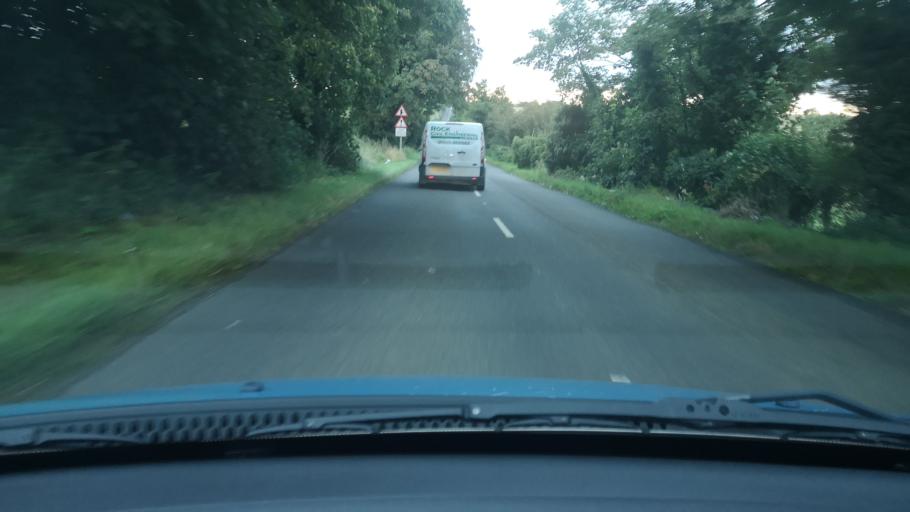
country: GB
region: England
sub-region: Doncaster
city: Campsall
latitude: 53.6174
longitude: -1.1995
